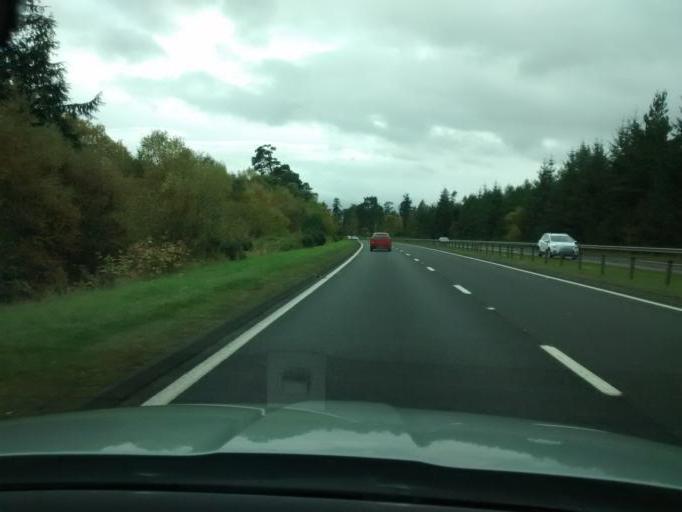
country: GB
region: Scotland
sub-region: Perth and Kinross
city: Methven
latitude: 56.3671
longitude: -3.5521
